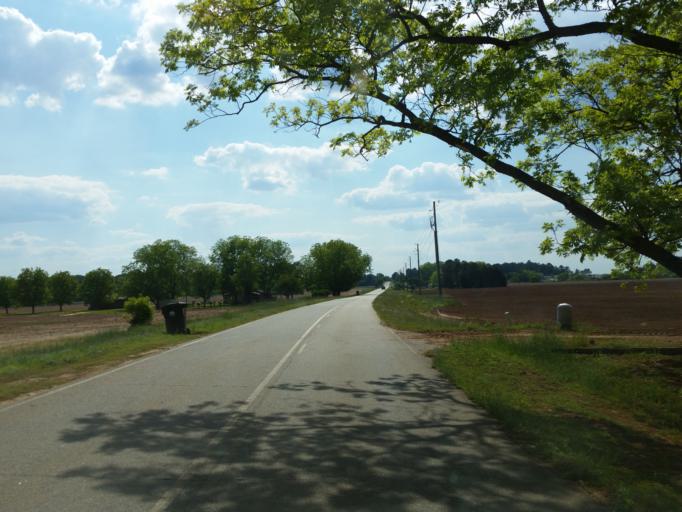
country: US
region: Georgia
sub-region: Houston County
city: Centerville
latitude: 32.5782
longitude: -83.7315
